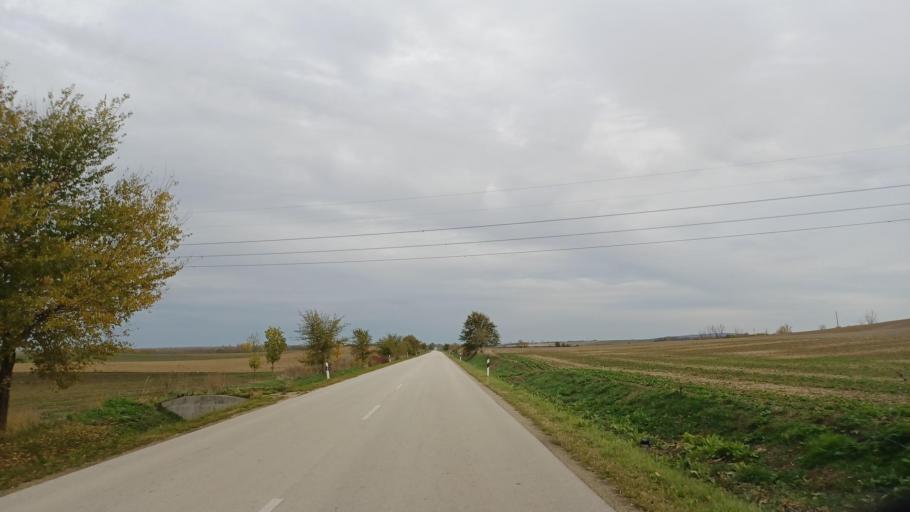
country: HU
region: Tolna
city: Nagydorog
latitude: 46.6703
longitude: 18.6025
